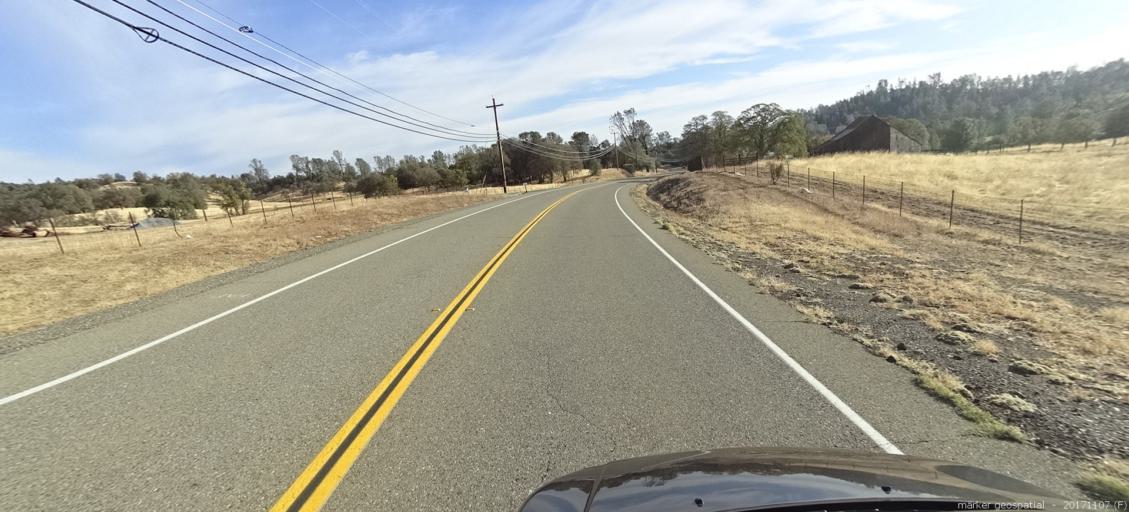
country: US
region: California
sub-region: Shasta County
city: Shasta
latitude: 40.5459
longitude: -122.4632
